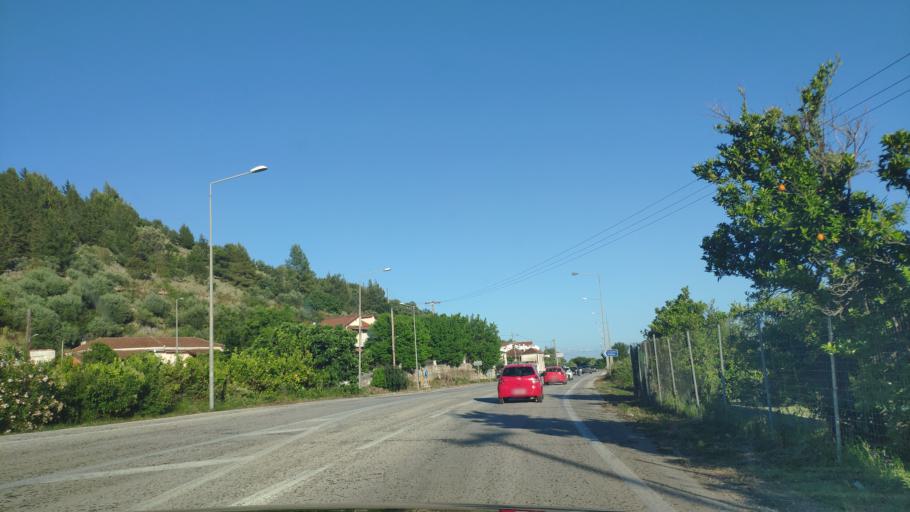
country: GR
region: Epirus
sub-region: Nomos Prevezis
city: Louros
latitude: 39.1775
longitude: 20.7885
